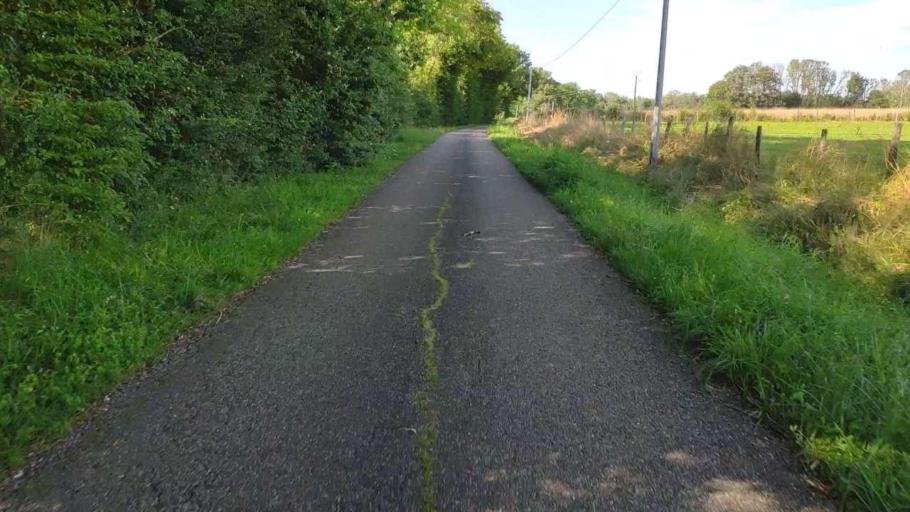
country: FR
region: Franche-Comte
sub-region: Departement du Jura
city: Bletterans
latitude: 46.8239
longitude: 5.5007
